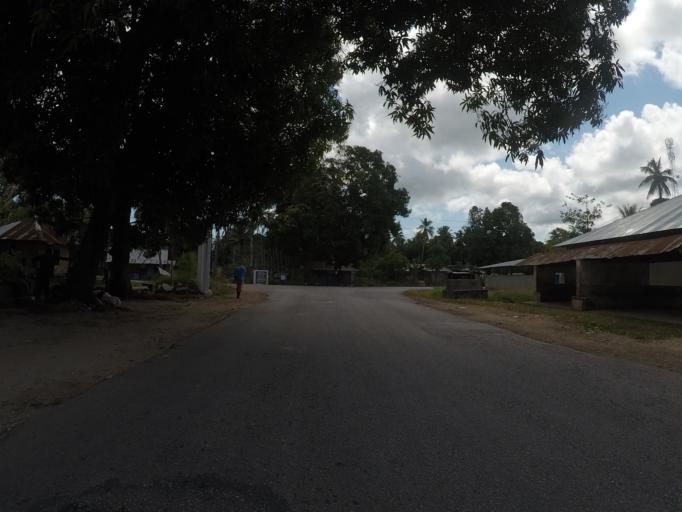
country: TZ
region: Zanzibar Central/South
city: Nganane
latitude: -6.2887
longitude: 39.4387
